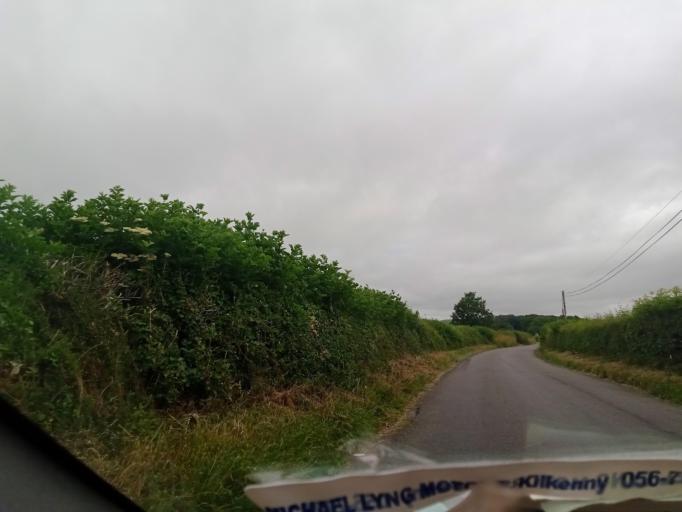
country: IE
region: Leinster
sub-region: Kilkenny
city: Ballyragget
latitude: 52.7369
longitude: -7.4159
